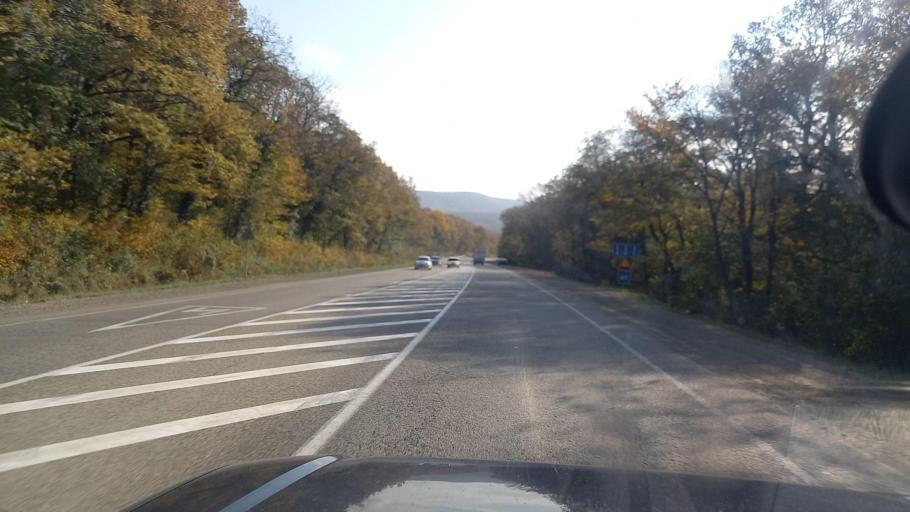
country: RU
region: Krasnodarskiy
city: Verkhnebakanskiy
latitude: 44.8431
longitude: 37.6985
